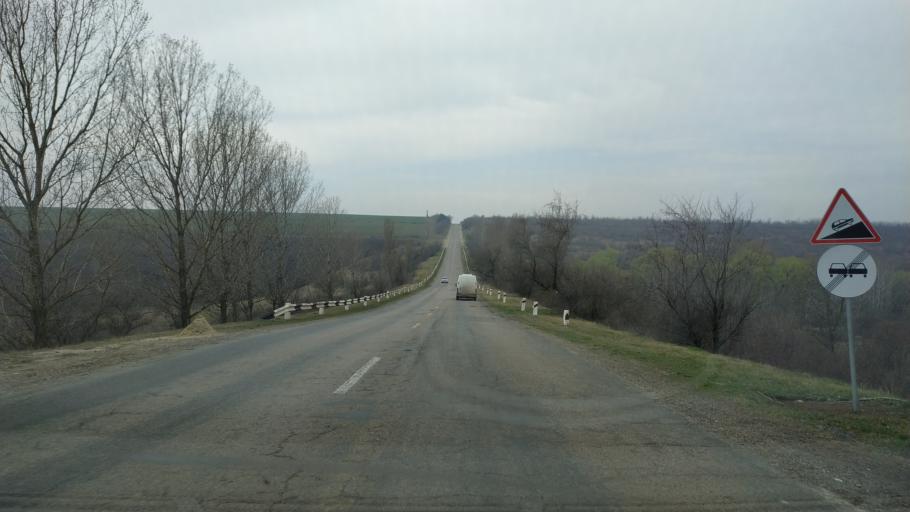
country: MD
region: Cahul
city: Cahul
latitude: 45.9593
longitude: 28.3818
